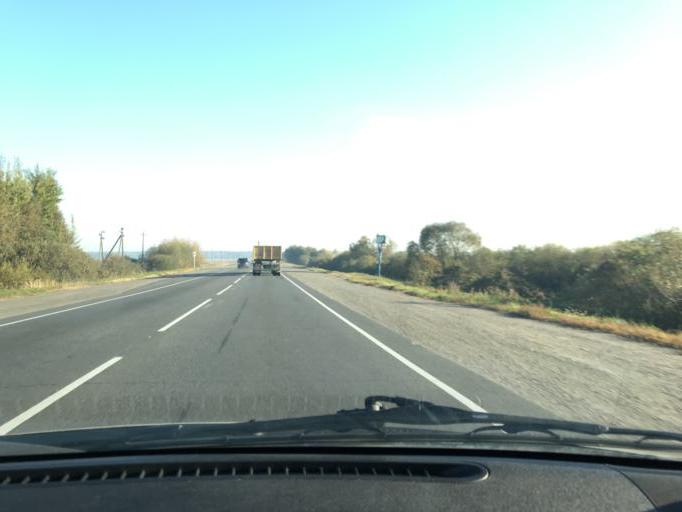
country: BY
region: Brest
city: Asnyezhytsy
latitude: 52.2156
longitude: 26.1260
